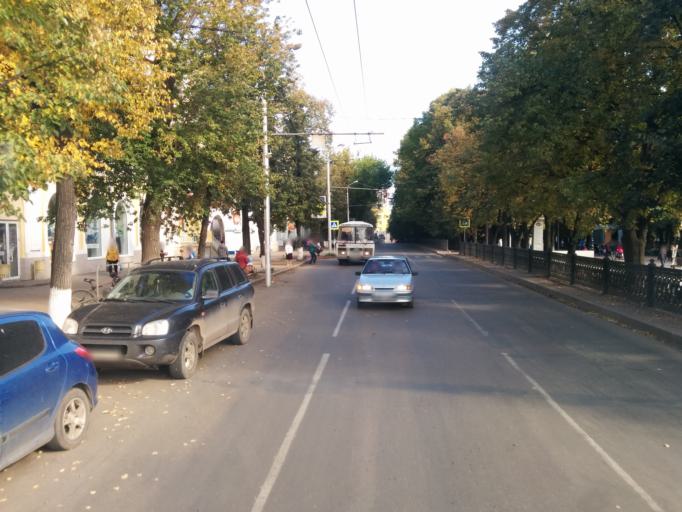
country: RU
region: Bashkortostan
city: Ufa
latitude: 54.8190
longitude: 56.0706
